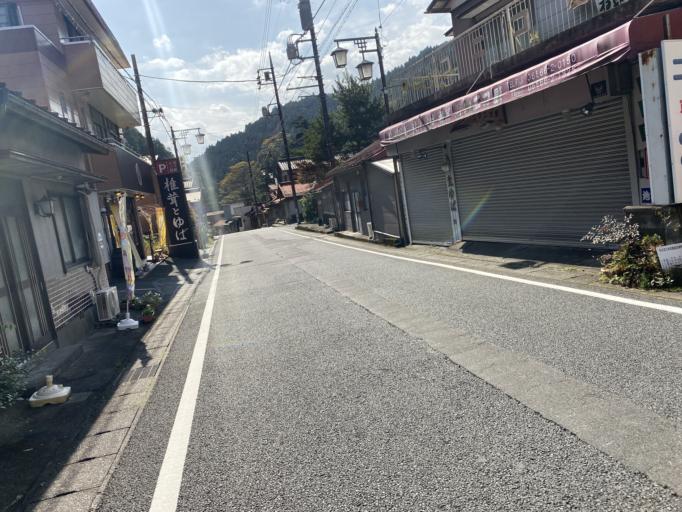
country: JP
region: Shizuoka
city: Fujinomiya
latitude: 35.3749
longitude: 138.4253
